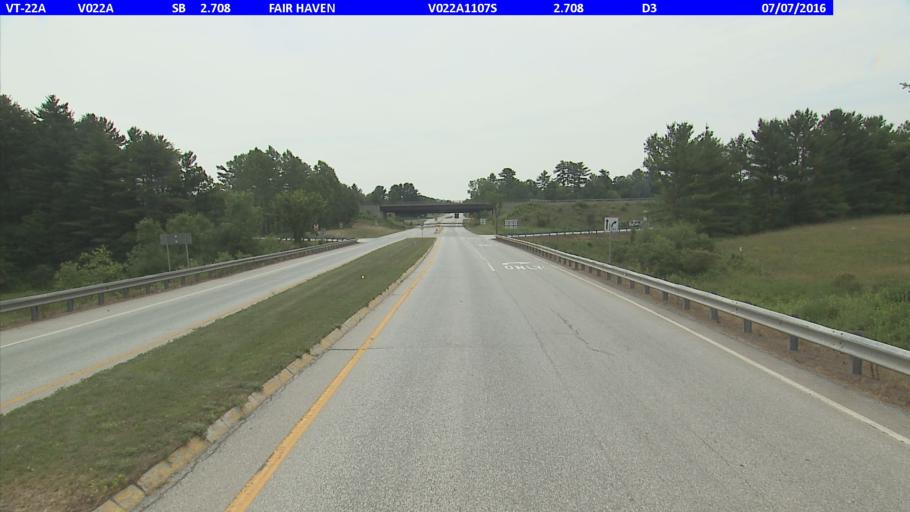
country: US
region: Vermont
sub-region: Rutland County
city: Fair Haven
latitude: 43.6075
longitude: -73.2799
